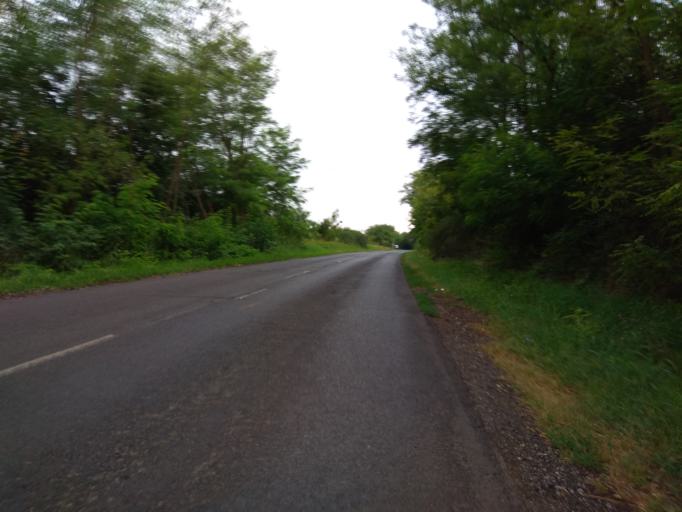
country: HU
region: Borsod-Abauj-Zemplen
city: Monok
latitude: 48.1747
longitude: 21.1096
